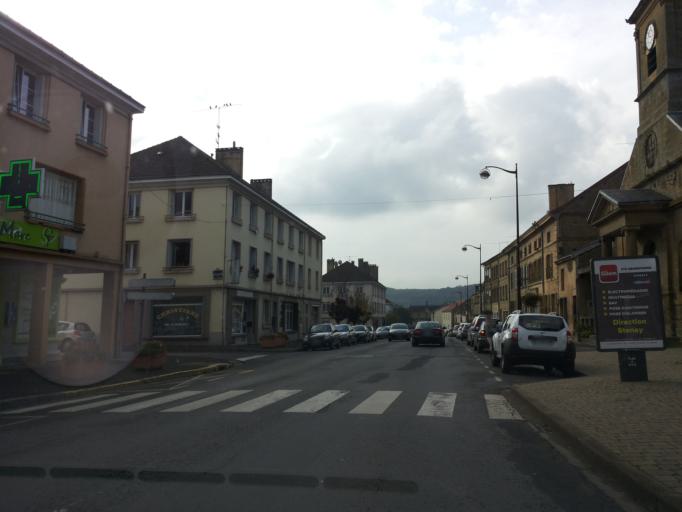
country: FR
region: Lorraine
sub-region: Departement de la Meuse
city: Montmedy
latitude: 49.5193
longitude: 5.3675
